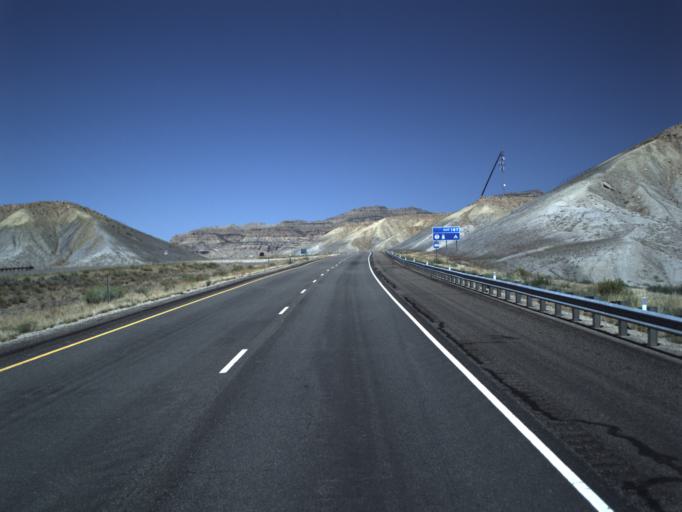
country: US
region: Utah
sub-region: Grand County
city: Moab
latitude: 38.9578
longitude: -109.7092
